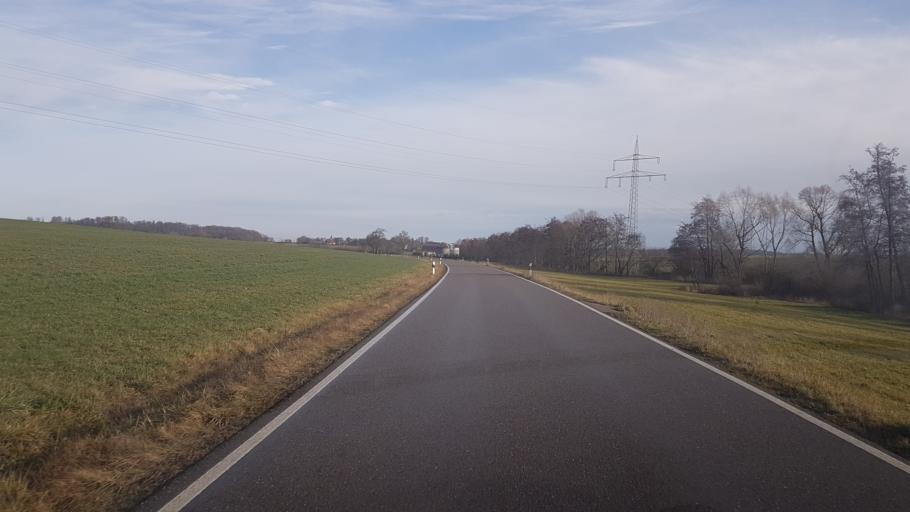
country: DE
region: Baden-Wuerttemberg
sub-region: Regierungsbezirk Stuttgart
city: Wolpertshausen
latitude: 49.2053
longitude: 9.8502
